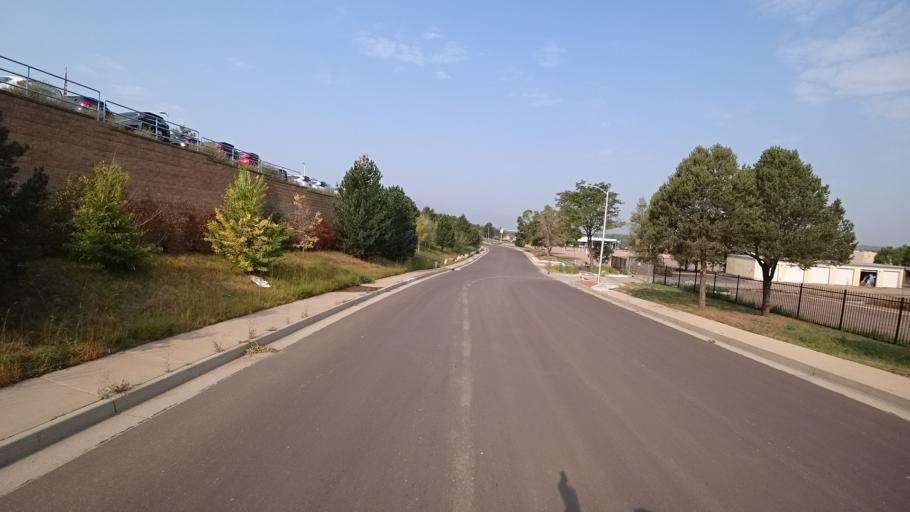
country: US
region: Colorado
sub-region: El Paso County
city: Stratmoor
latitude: 38.8179
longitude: -104.7547
